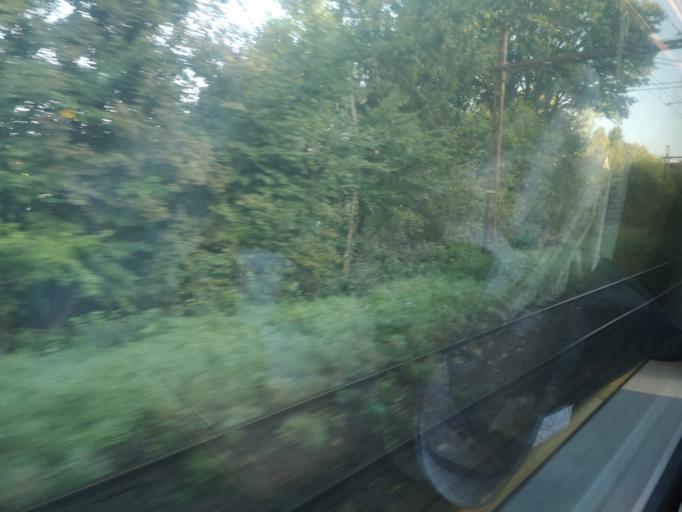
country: SE
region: Skane
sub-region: Hassleholms Kommun
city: Hastveda
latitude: 56.2897
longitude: 13.9353
